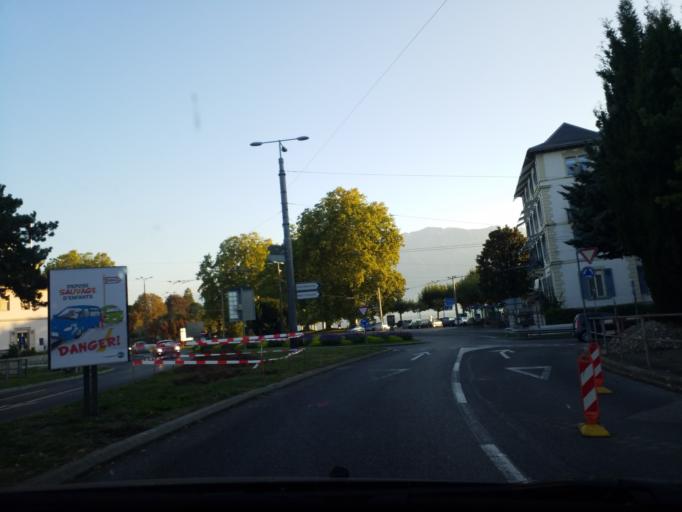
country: CH
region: Vaud
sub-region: Riviera-Pays-d'Enhaut District
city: La Tour-de-Peilz
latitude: 46.4580
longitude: 6.8527
